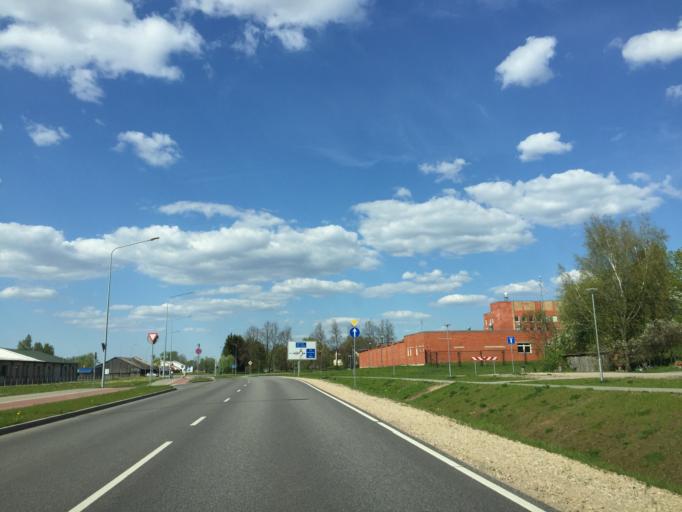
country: LV
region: Limbazu Rajons
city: Limbazi
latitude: 57.5110
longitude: 24.7237
